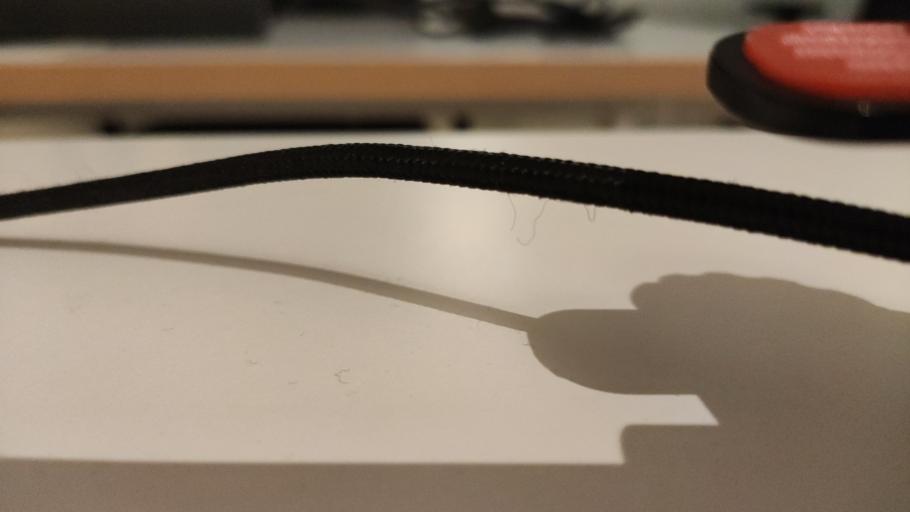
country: RU
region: Moskovskaya
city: Novoye
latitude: 55.6617
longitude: 38.9408
